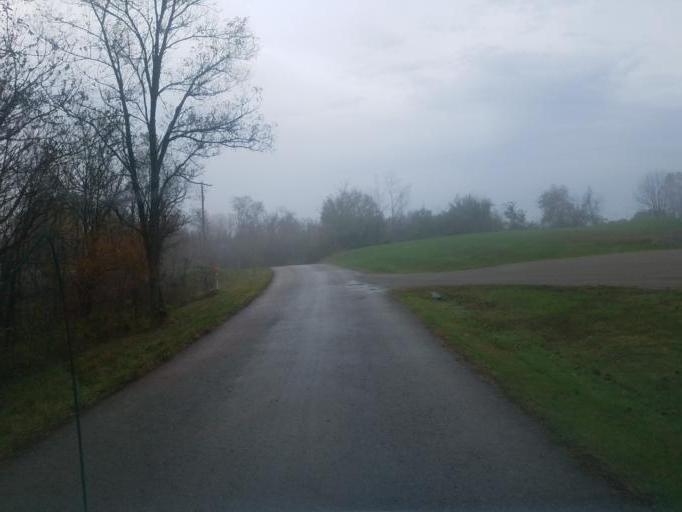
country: US
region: Ohio
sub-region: Morgan County
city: McConnelsville
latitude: 39.4979
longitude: -81.8171
